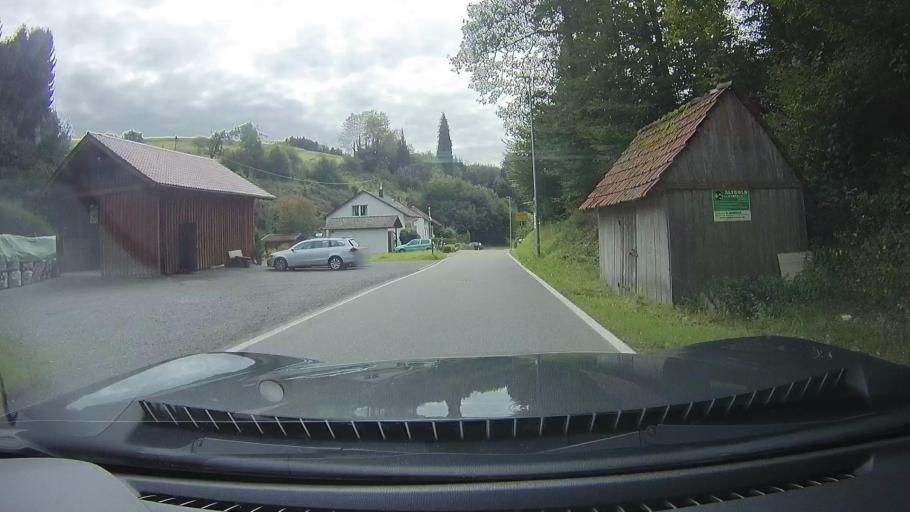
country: DE
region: Baden-Wuerttemberg
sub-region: Regierungsbezirk Stuttgart
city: Wustenrot
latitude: 49.0848
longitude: 9.4332
